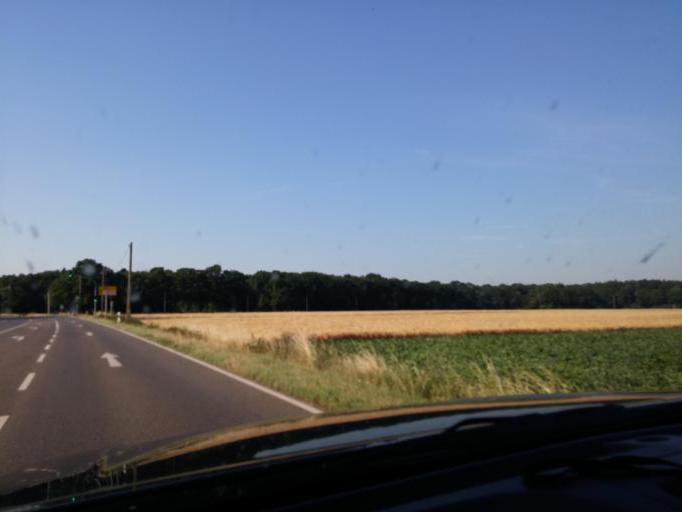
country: DE
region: North Rhine-Westphalia
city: Wegberg
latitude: 51.1811
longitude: 6.3415
